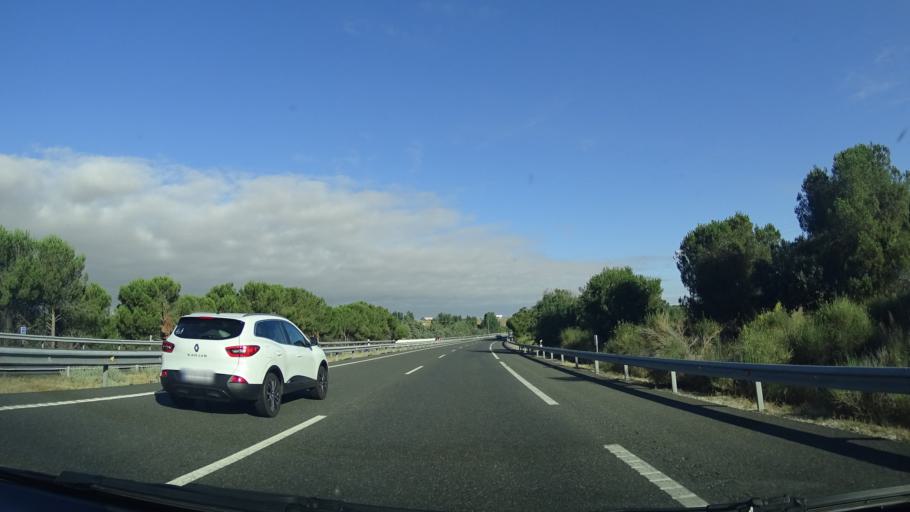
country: ES
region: Castille and Leon
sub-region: Provincia de Avila
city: Sanchidrian
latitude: 40.8623
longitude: -4.5603
